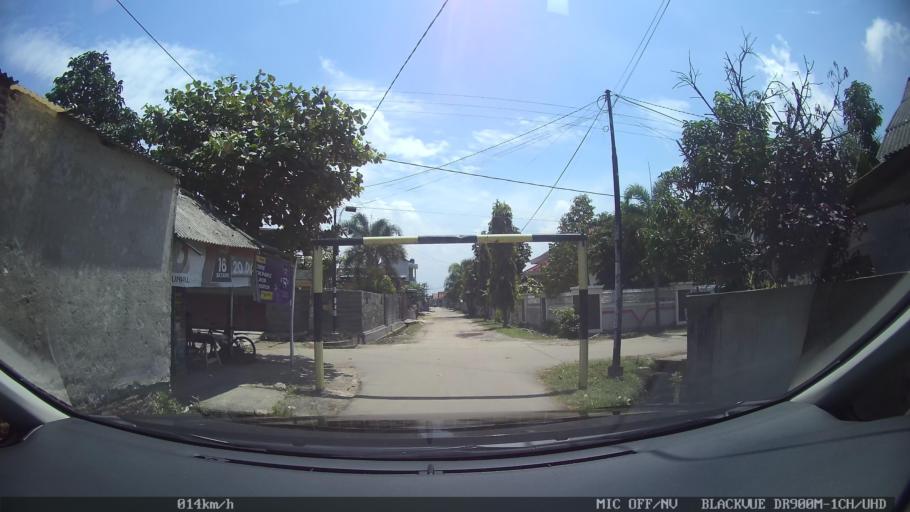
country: ID
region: Lampung
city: Kedaton
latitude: -5.3763
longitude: 105.2924
